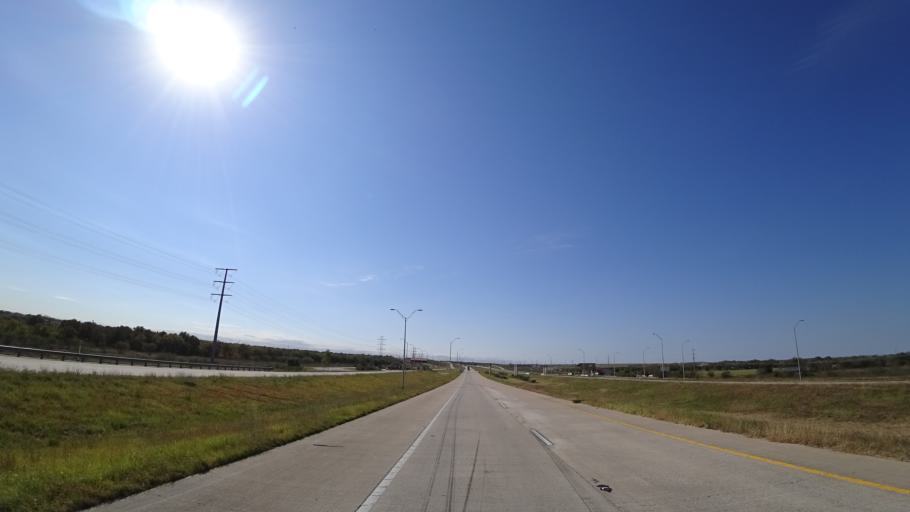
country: US
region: Texas
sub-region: Travis County
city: Garfield
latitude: 30.1716
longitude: -97.6421
